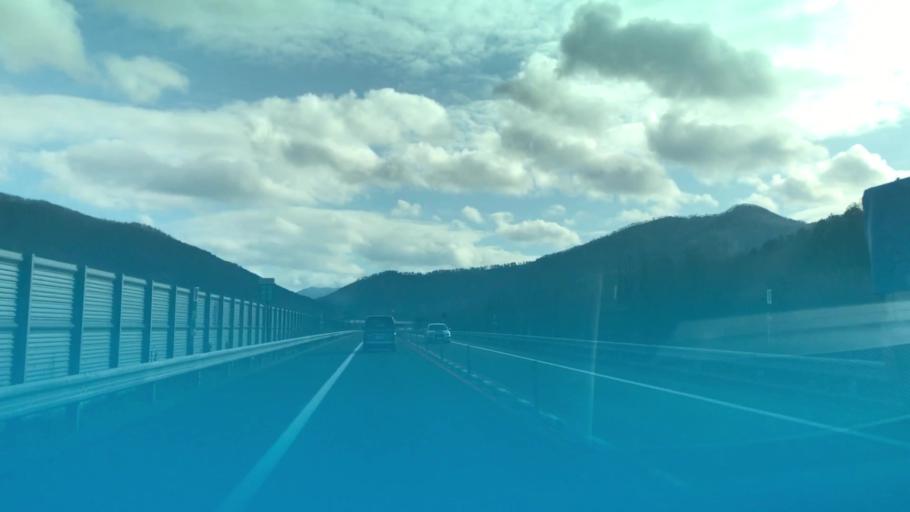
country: JP
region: Hokkaido
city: Shimo-furano
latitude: 43.0632
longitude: 142.5473
